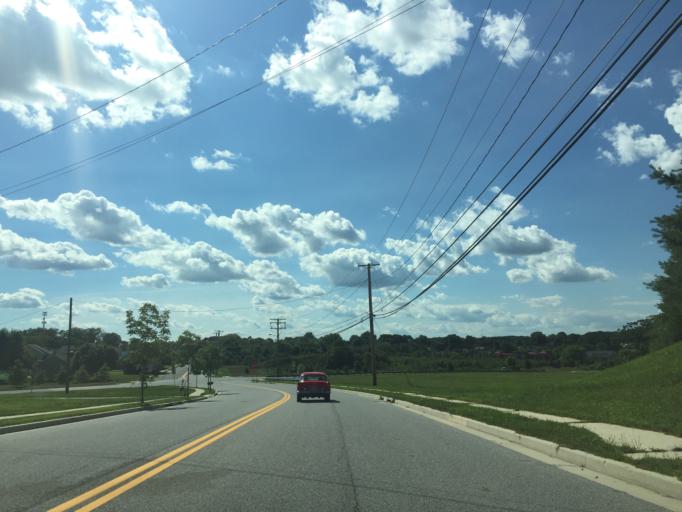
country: US
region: Maryland
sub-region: Baltimore County
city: Perry Hall
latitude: 39.4165
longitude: -76.4519
